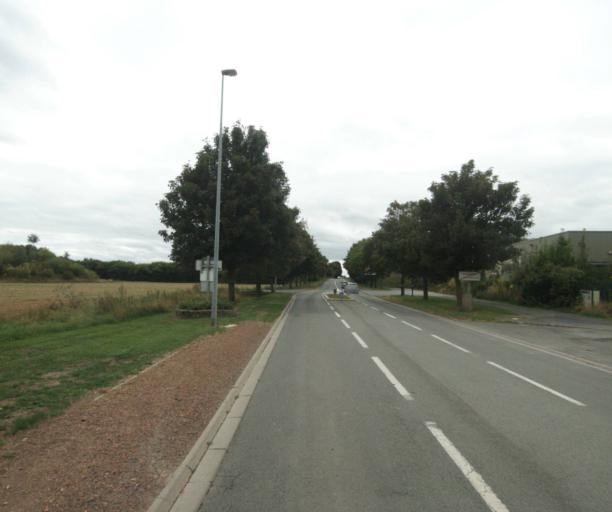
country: FR
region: Nord-Pas-de-Calais
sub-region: Departement du Nord
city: Sainghin-en-Melantois
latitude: 50.5667
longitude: 3.1640
